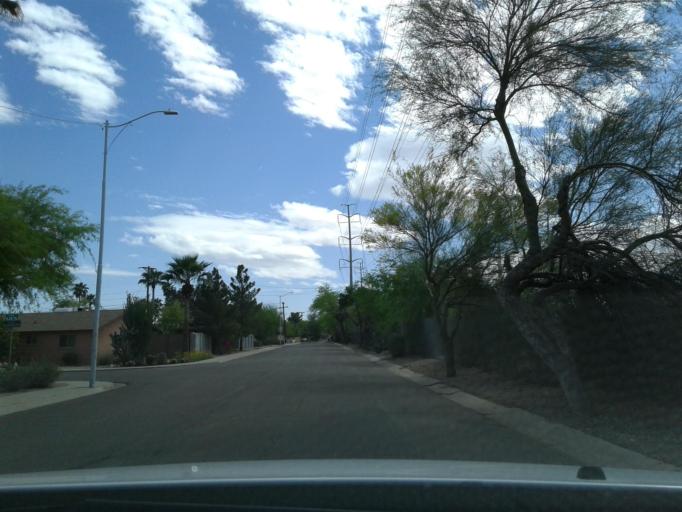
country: US
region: Arizona
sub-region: Maricopa County
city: Scottsdale
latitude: 33.4749
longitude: -111.9390
